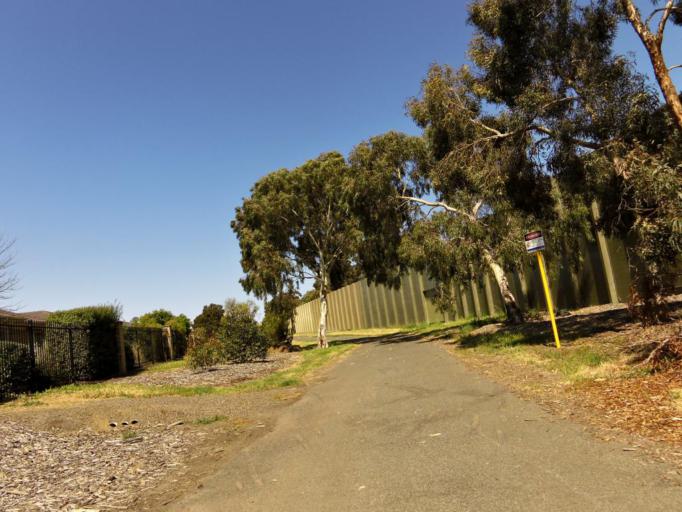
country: AU
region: Victoria
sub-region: Moreland
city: Gowanbrae
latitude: -37.7076
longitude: 144.8908
